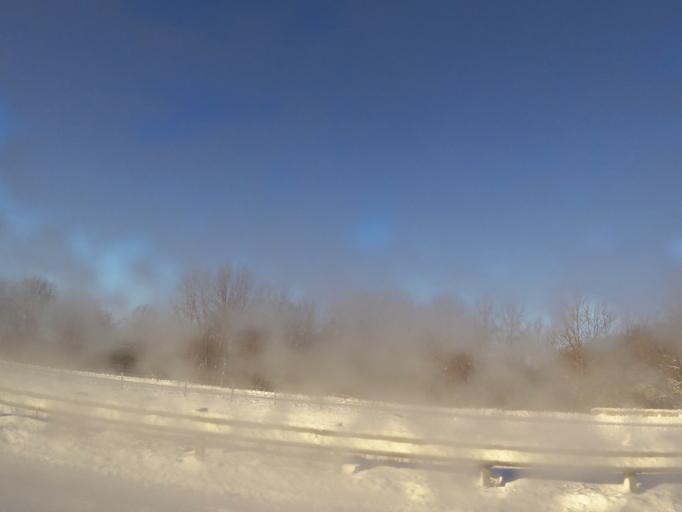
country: US
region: Minnesota
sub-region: Steele County
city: Owatonna
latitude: 44.0324
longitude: -93.2470
